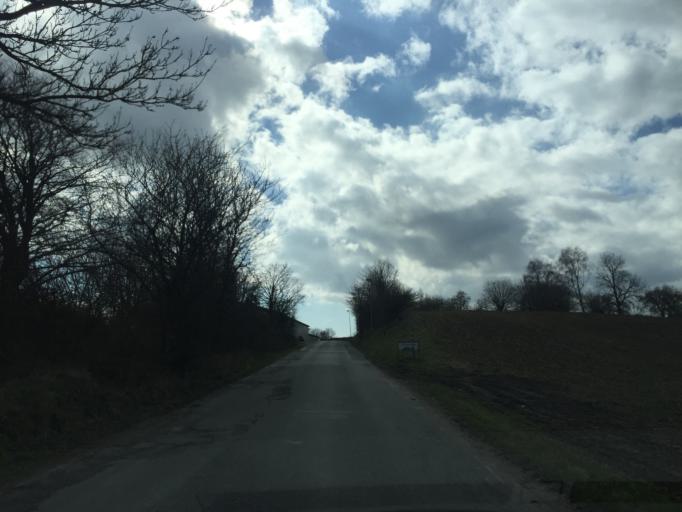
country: DK
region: South Denmark
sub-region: Svendborg Kommune
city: Svendborg
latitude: 55.0767
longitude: 10.4974
